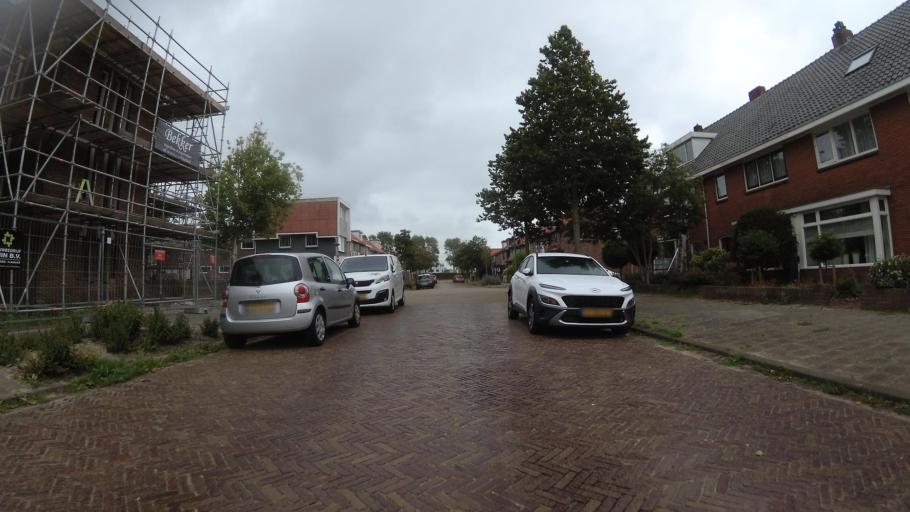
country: NL
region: North Holland
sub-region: Gemeente Den Helder
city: Den Helder
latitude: 52.9539
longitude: 4.7593
